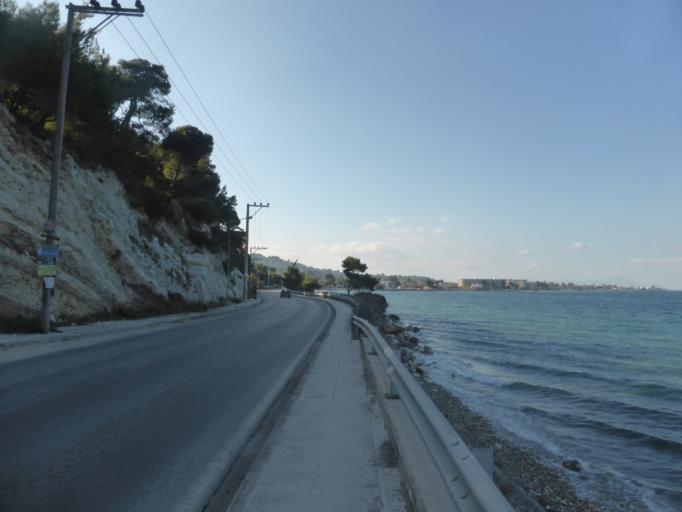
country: GR
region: Attica
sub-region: Nomarchia Anatolikis Attikis
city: Markopoulo Oropou
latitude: 38.3122
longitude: 23.8382
